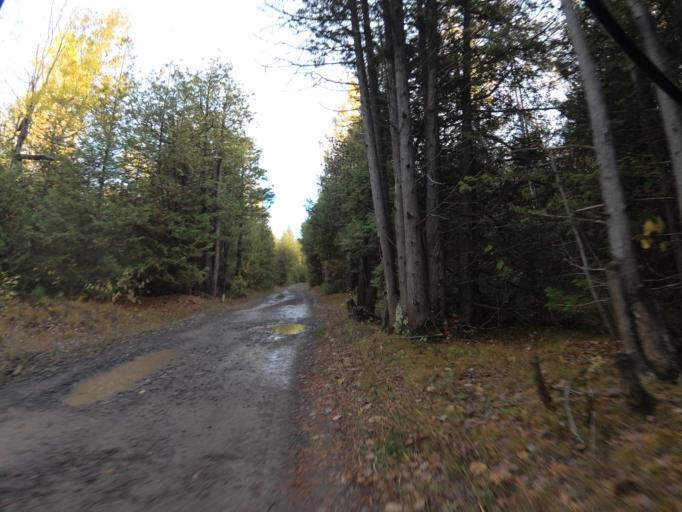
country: CA
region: Ontario
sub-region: Lanark County
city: Smiths Falls
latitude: 45.0088
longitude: -75.8009
